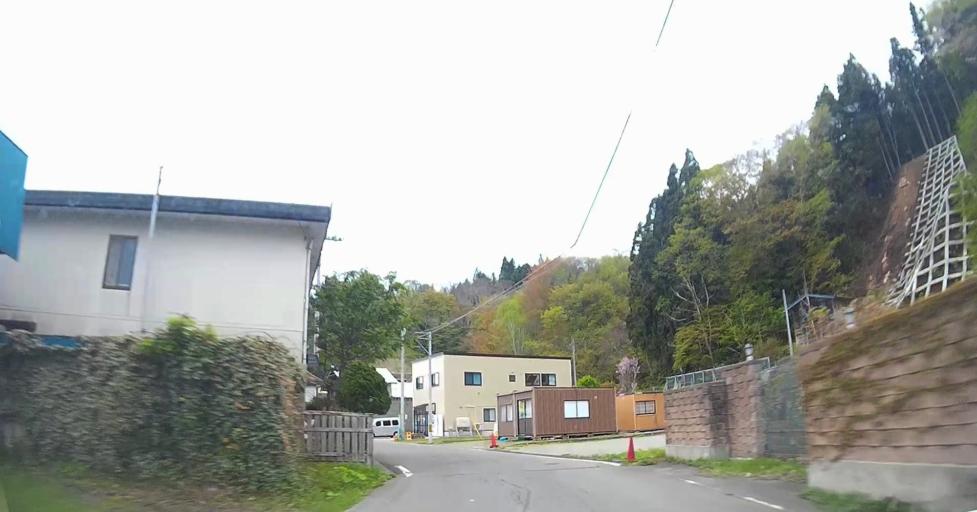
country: JP
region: Aomori
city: Shimokizukuri
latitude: 41.1974
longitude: 140.4300
